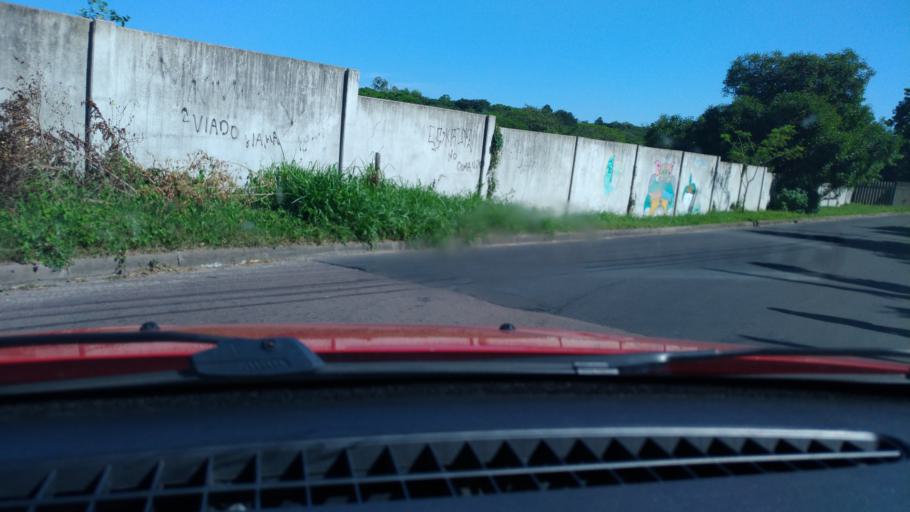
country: BR
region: Rio Grande do Sul
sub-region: Cachoeirinha
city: Cachoeirinha
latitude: -30.0348
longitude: -51.1277
